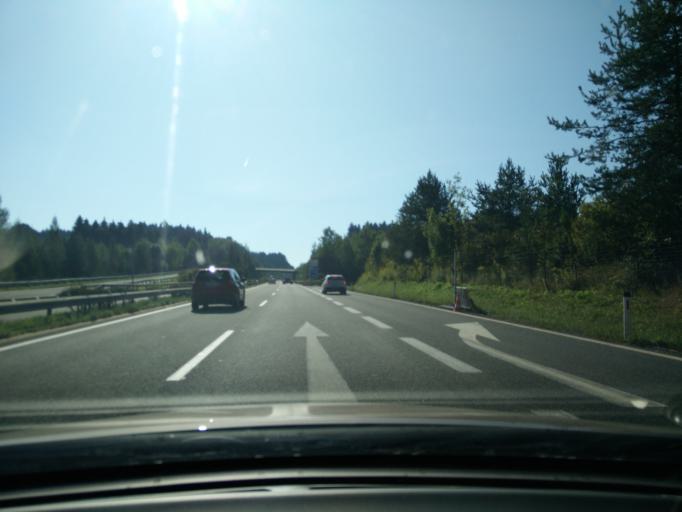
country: AT
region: Carinthia
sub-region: Politischer Bezirk Villach Land
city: Rosegg
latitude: 46.5805
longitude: 13.9940
